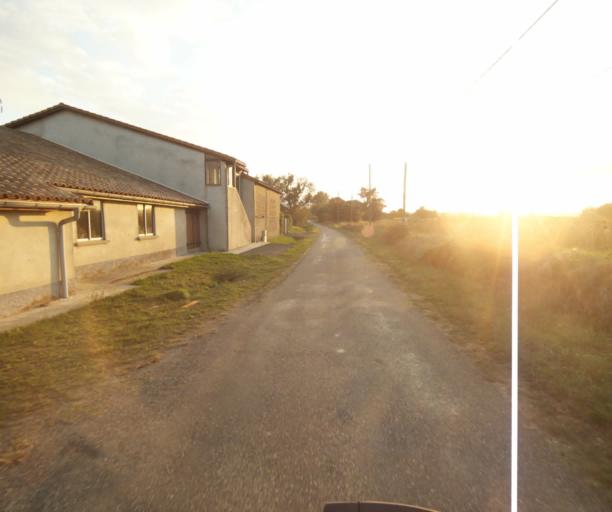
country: FR
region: Midi-Pyrenees
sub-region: Departement du Tarn-et-Garonne
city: Verdun-sur-Garonne
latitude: 43.8203
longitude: 1.2040
